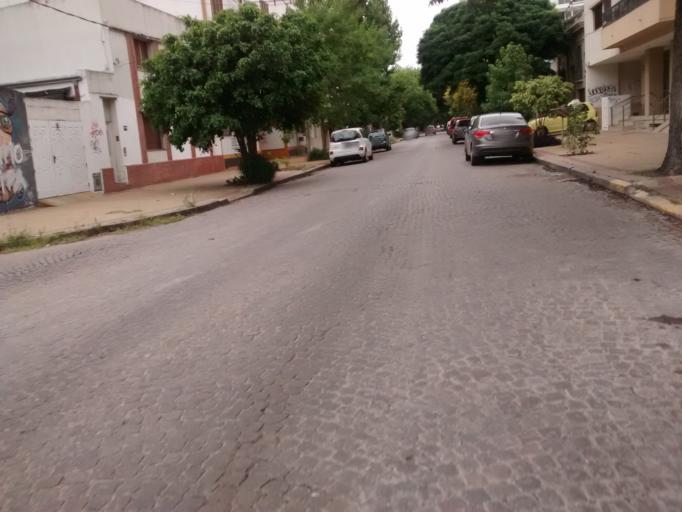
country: AR
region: Buenos Aires
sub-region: Partido de La Plata
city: La Plata
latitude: -34.9262
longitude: -57.9369
